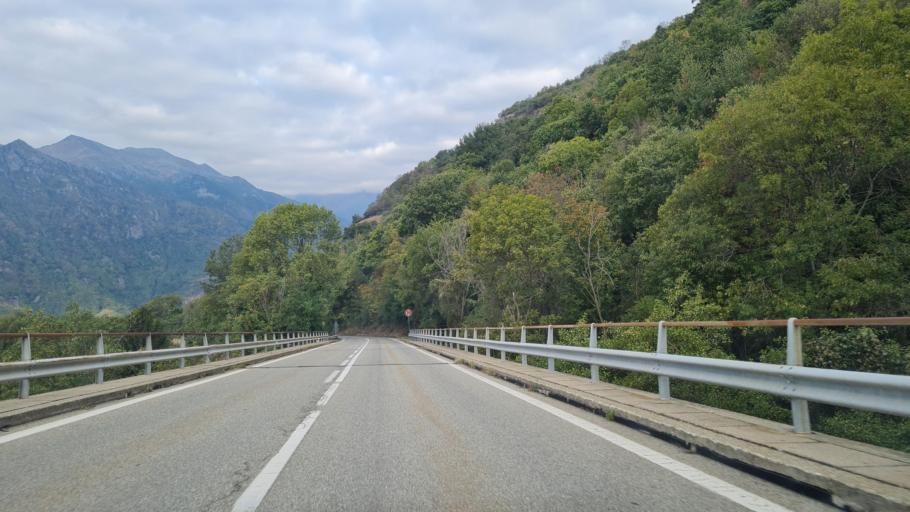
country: IT
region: Piedmont
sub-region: Provincia di Torino
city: Andrate
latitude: 45.5208
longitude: 7.8730
